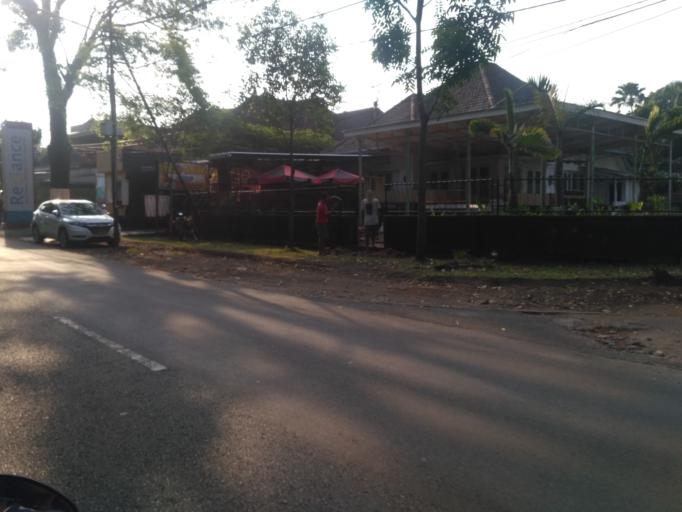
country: ID
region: East Java
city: Malang
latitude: -7.9683
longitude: 112.6268
